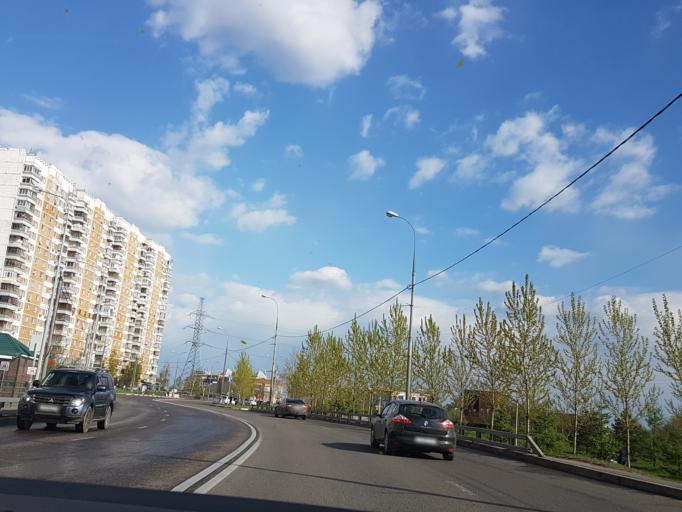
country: RU
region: Moskovskaya
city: Pavshino
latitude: 55.8379
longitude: 37.3790
